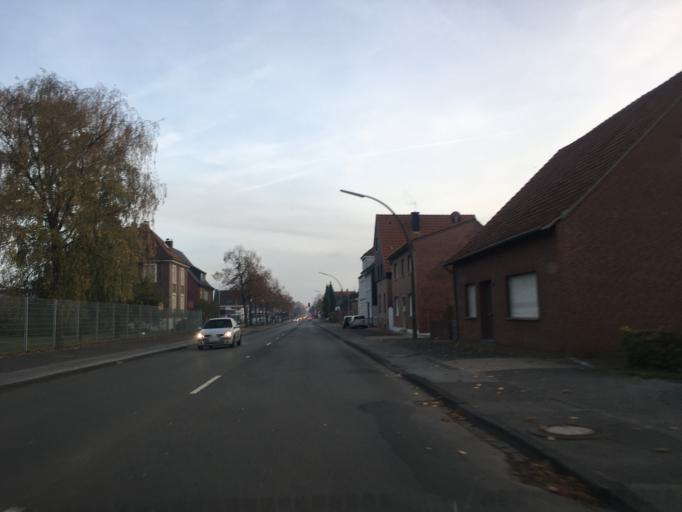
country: DE
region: North Rhine-Westphalia
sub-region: Regierungsbezirk Munster
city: Steinfurt
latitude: 52.1163
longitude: 7.3973
